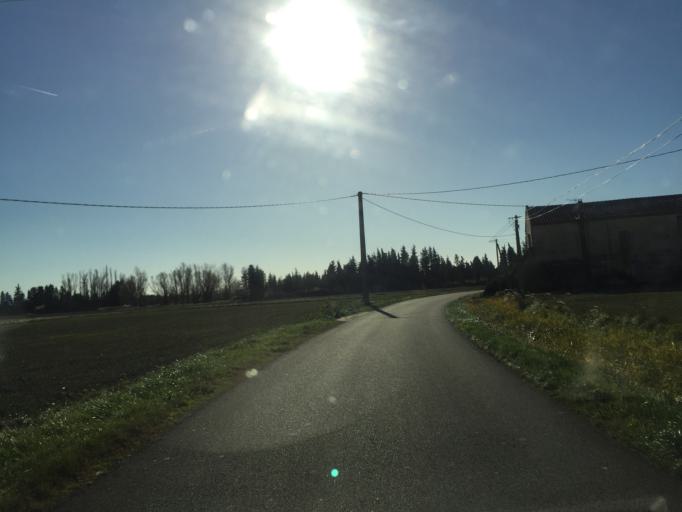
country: FR
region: Provence-Alpes-Cote d'Azur
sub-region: Departement du Vaucluse
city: Bedarrides
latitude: 44.0581
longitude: 4.9078
